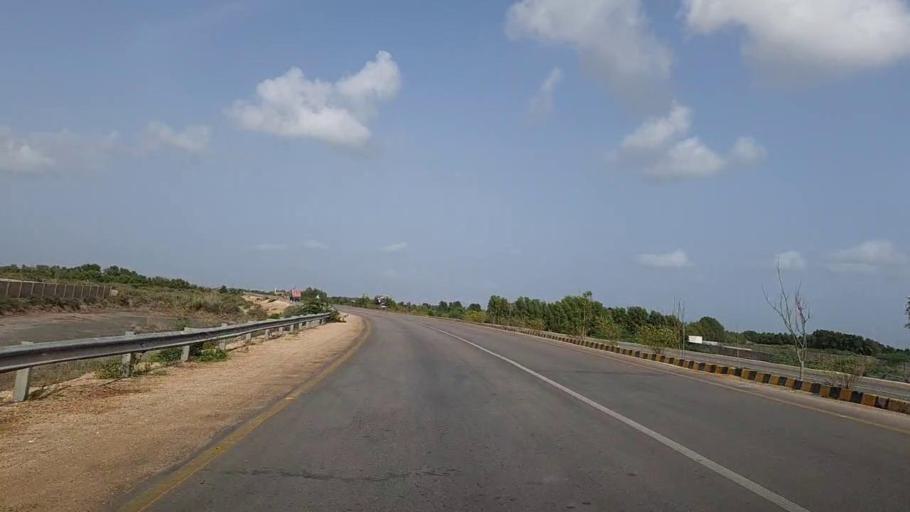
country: PK
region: Sindh
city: Gharo
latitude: 24.7297
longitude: 67.6069
